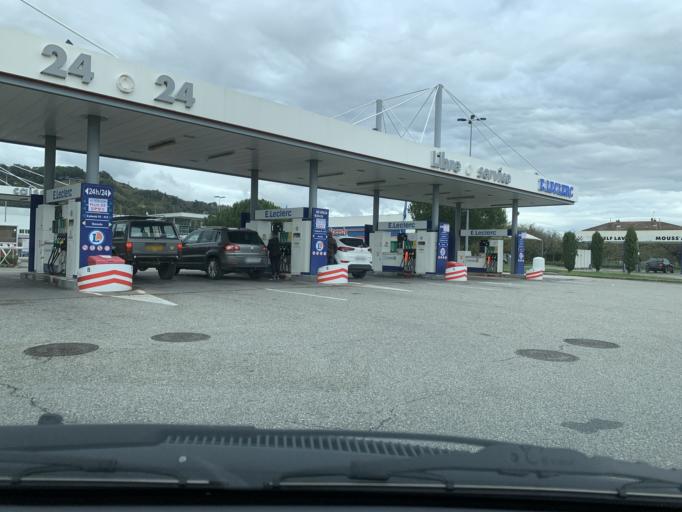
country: FR
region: Rhone-Alpes
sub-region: Departement de l'Isere
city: Saint-Marcellin
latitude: 45.1441
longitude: 5.3055
